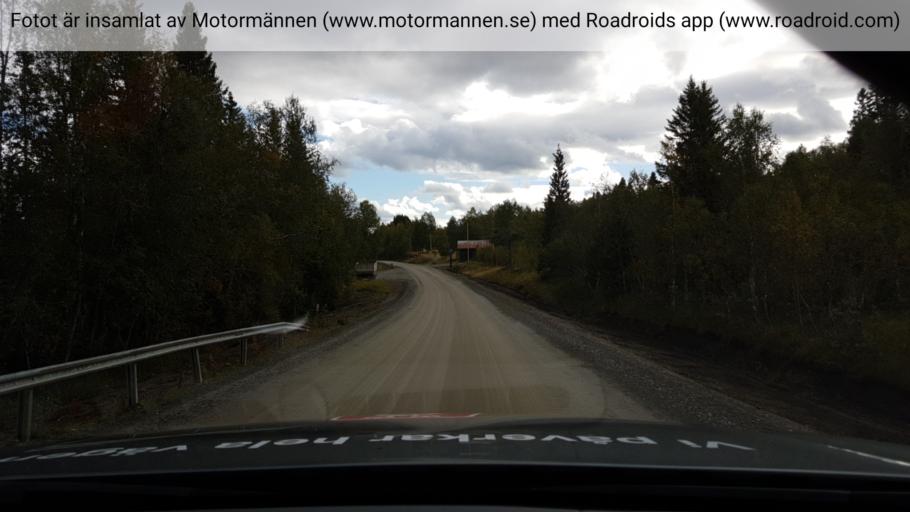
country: SE
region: Jaemtland
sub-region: Are Kommun
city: Are
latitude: 63.7132
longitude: 12.6272
